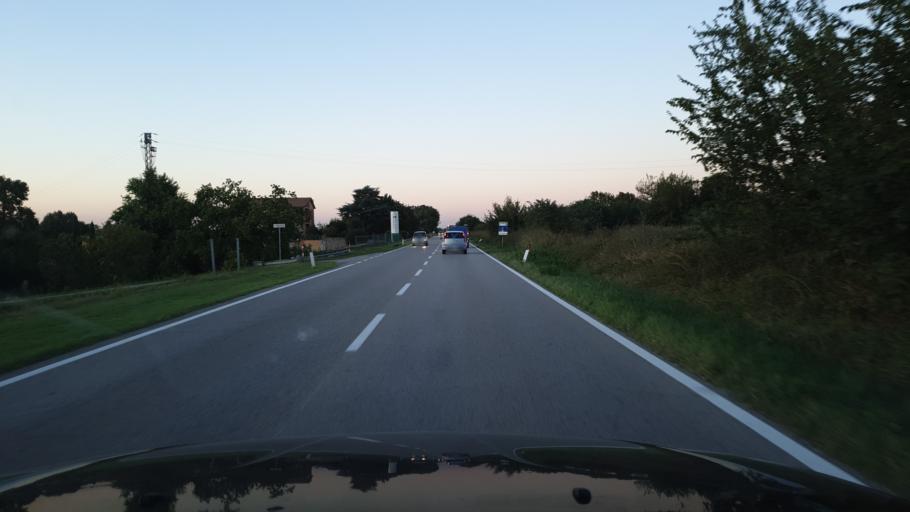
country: IT
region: Emilia-Romagna
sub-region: Provincia di Bologna
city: Ca De Fabbri
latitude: 44.6059
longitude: 11.4436
